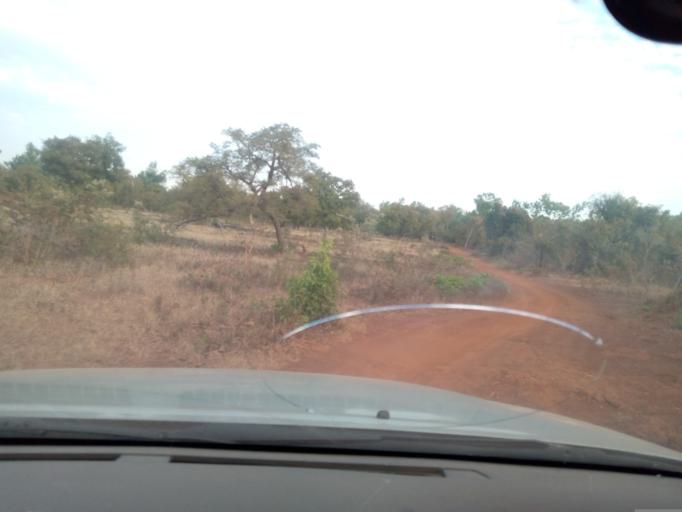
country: ML
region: Sikasso
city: Kadiolo
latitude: 10.5819
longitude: -5.8411
